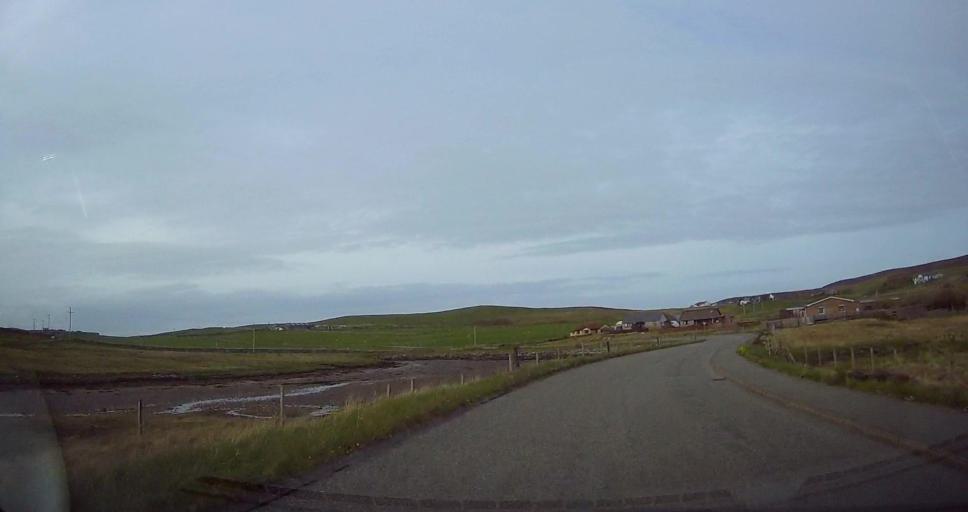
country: GB
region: Scotland
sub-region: Shetland Islands
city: Shetland
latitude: 60.1563
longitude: -1.1154
